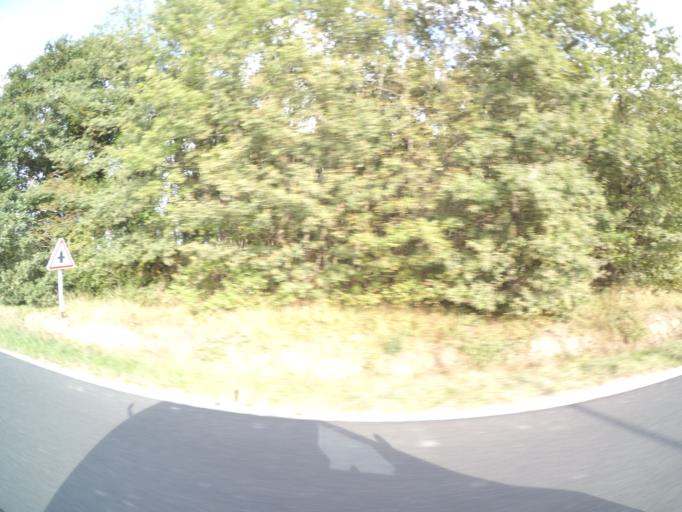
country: FR
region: Centre
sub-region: Departement d'Indre-et-Loire
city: Nazelles-Negron
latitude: 47.4694
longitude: 0.9545
